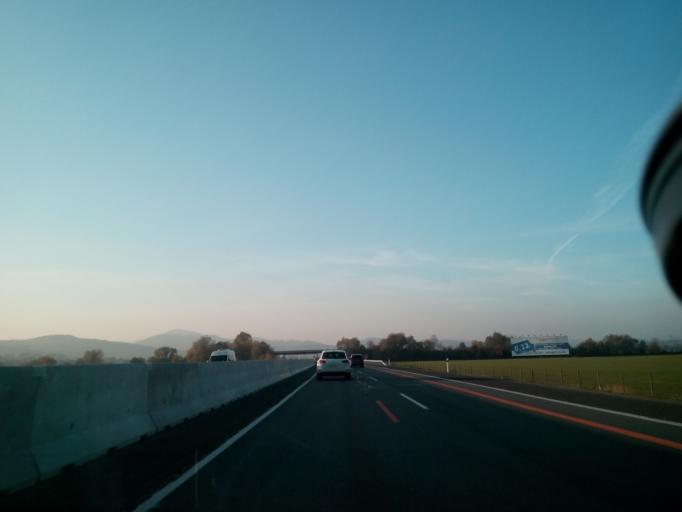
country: SK
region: Kosicky
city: Kosice
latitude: 48.8458
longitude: 21.2916
